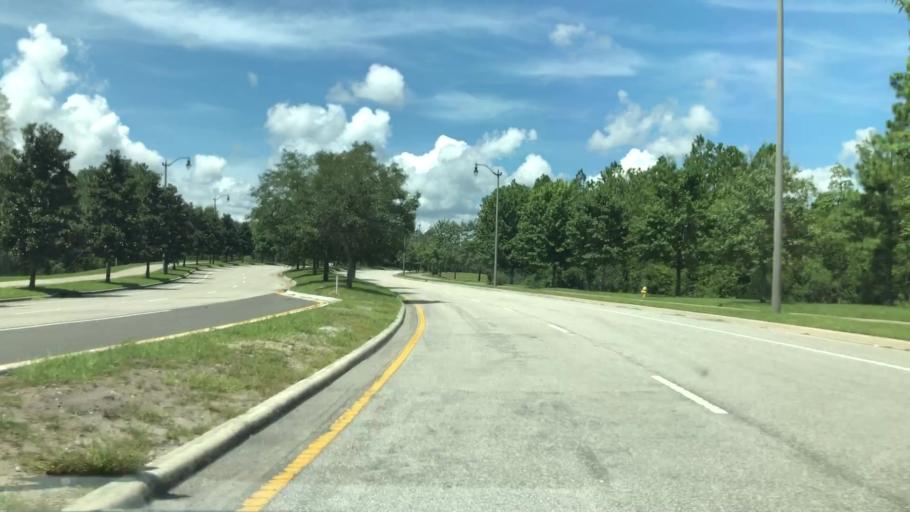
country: US
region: Florida
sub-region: Saint Johns County
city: Palm Valley
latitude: 30.1066
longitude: -81.4338
